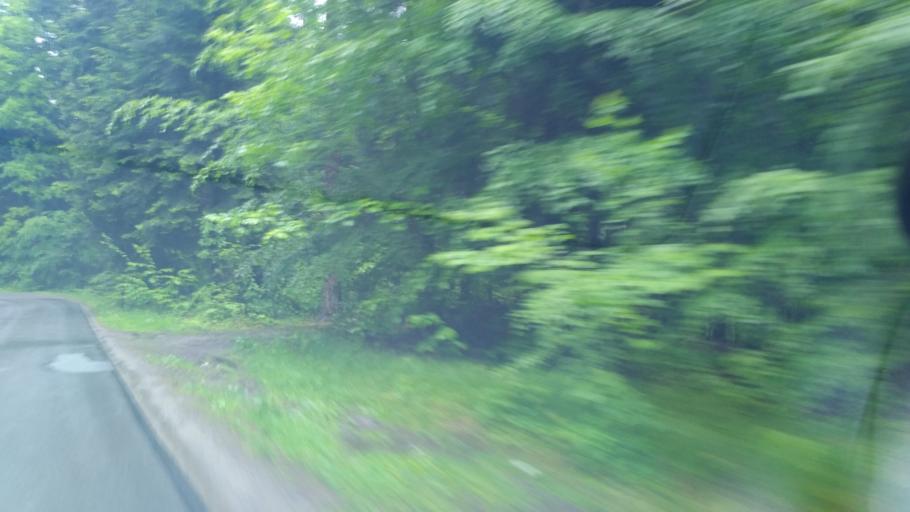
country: PL
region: Subcarpathian Voivodeship
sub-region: Powiat jasielski
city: Jaslo
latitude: 49.7771
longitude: 21.4950
